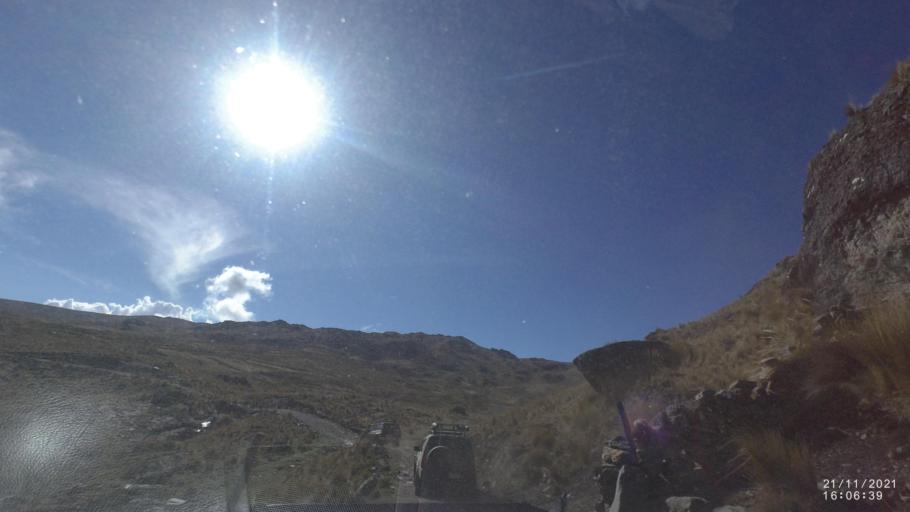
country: BO
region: Cochabamba
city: Cochabamba
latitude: -16.9911
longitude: -66.2639
